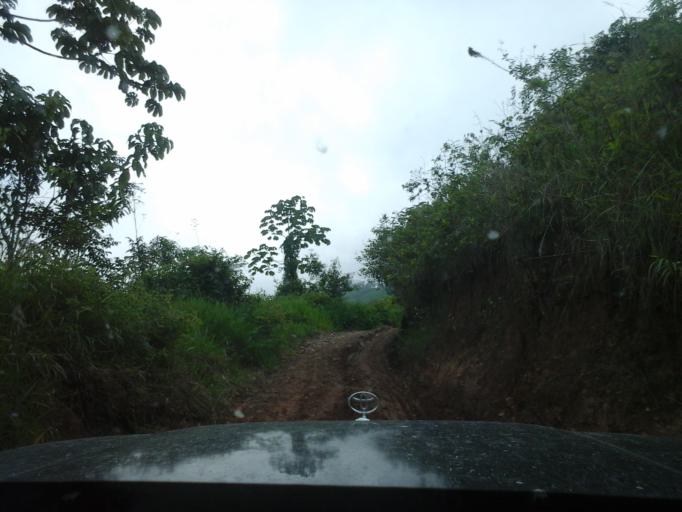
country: CO
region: Cesar
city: Agustin Codazzi
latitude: 9.9538
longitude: -73.0677
